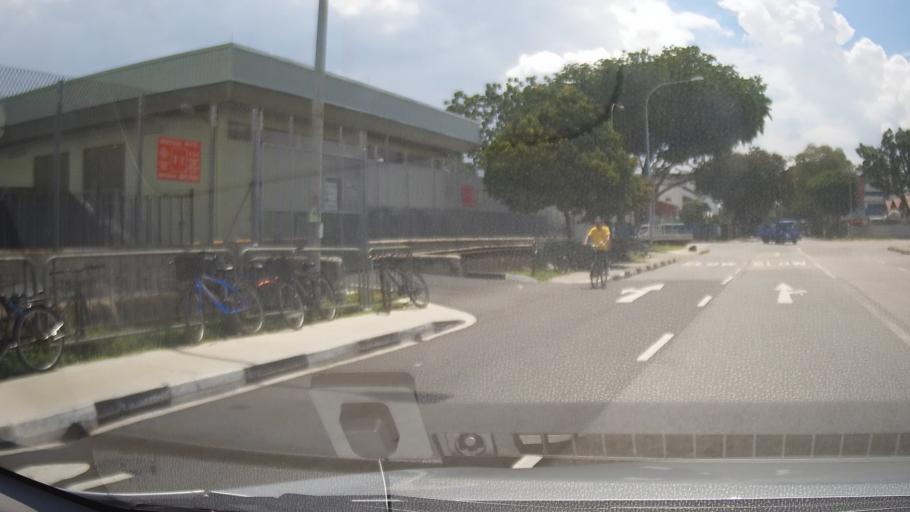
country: MY
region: Johor
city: Johor Bahru
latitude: 1.3292
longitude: 103.6944
